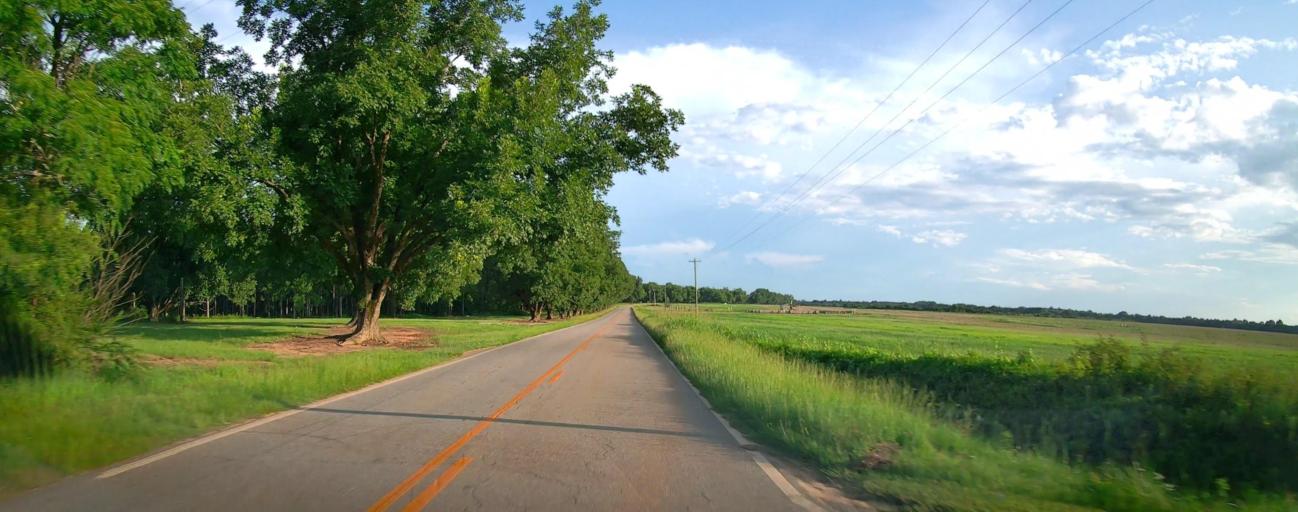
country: US
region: Georgia
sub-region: Peach County
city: Byron
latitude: 32.6575
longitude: -83.8608
